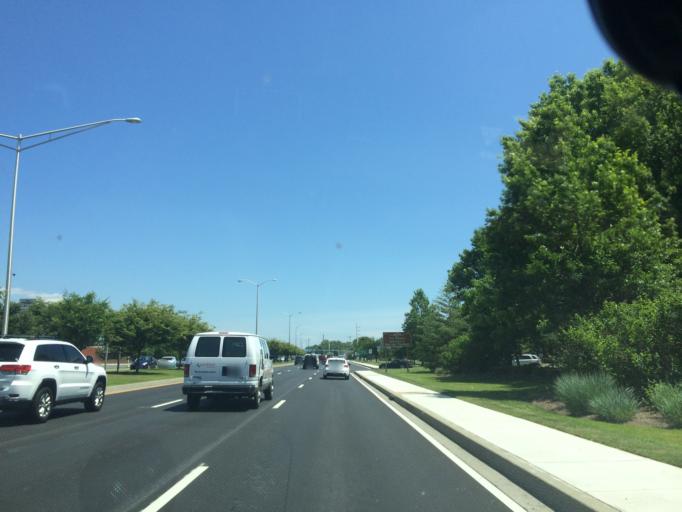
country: US
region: Maryland
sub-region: Dorchester County
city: Cambridge
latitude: 38.5599
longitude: -76.0634
